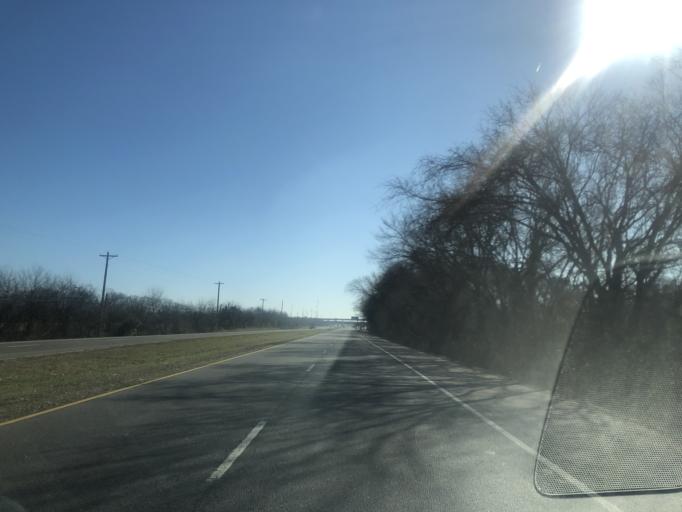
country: US
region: Tennessee
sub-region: Rutherford County
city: Smyrna
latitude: 35.9122
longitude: -86.4571
